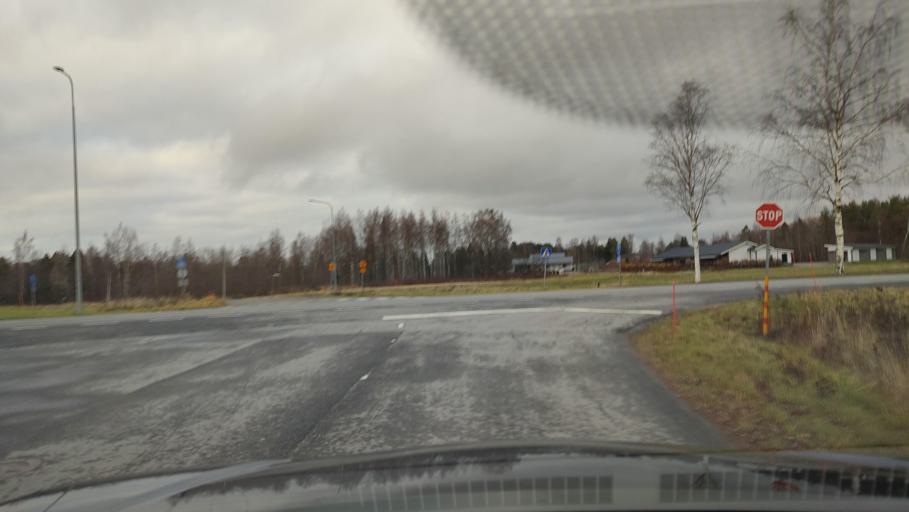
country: FI
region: Southern Ostrobothnia
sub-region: Suupohja
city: Kauhajoki
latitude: 62.4171
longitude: 22.1849
